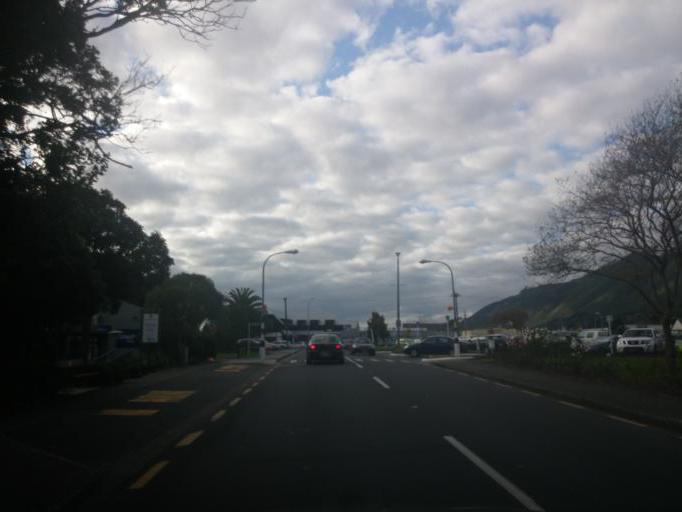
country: NZ
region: Wellington
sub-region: Kapiti Coast District
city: Paraparaumu
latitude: -40.8764
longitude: 175.0635
